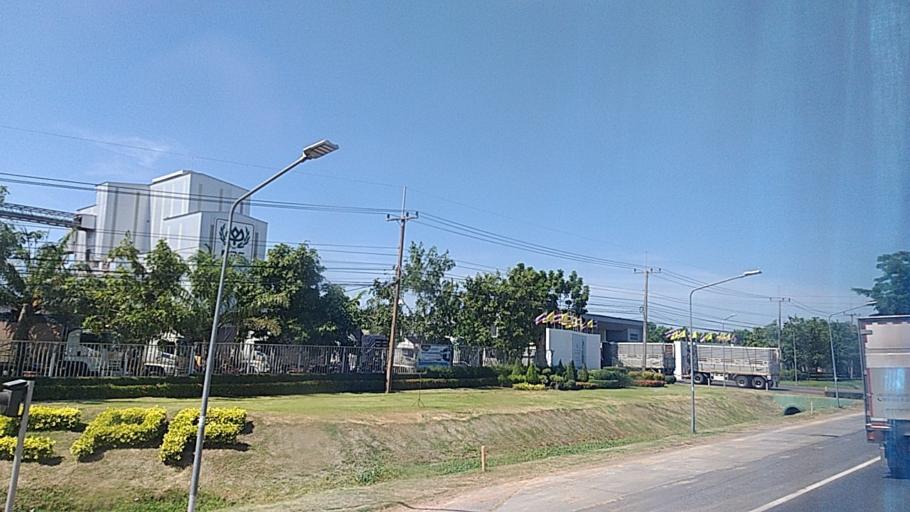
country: TH
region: Khon Kaen
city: Ban Haet
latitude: 16.2864
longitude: 102.7857
